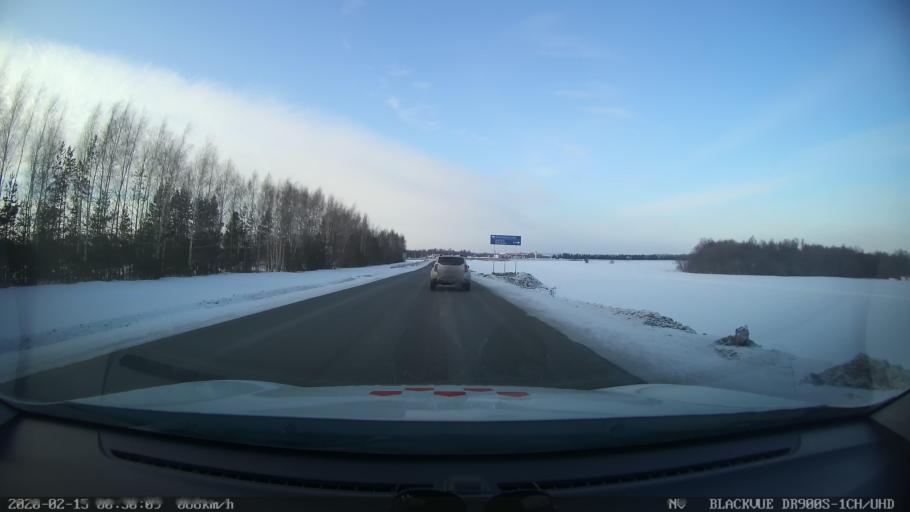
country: RU
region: Tatarstan
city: Verkhniy Uslon
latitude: 55.6569
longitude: 48.8605
